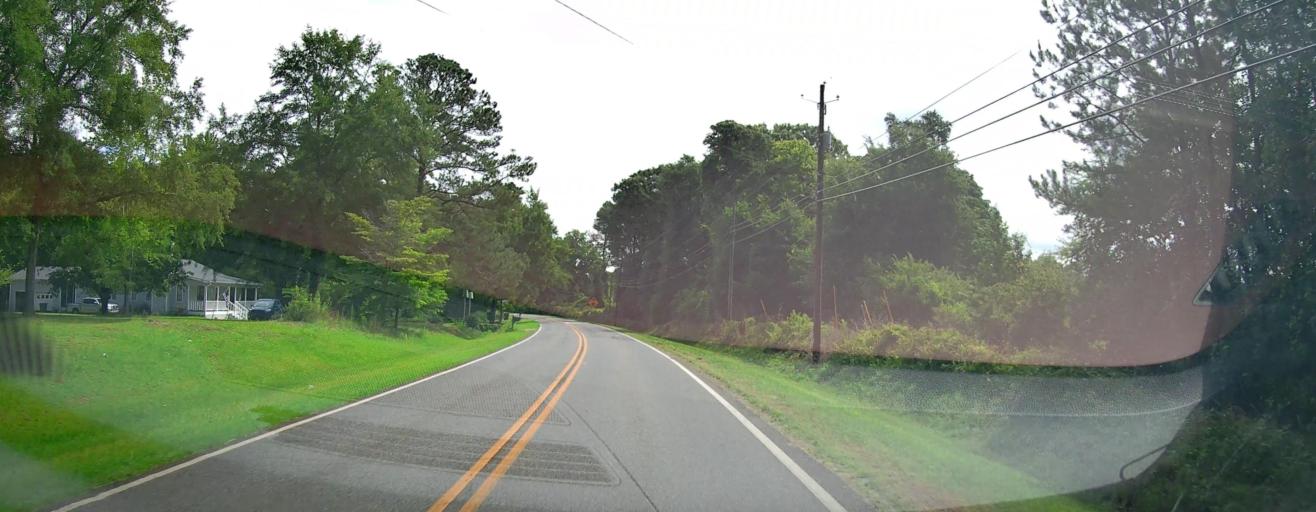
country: US
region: Georgia
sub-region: Peach County
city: Byron
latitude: 32.6491
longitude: -83.7661
